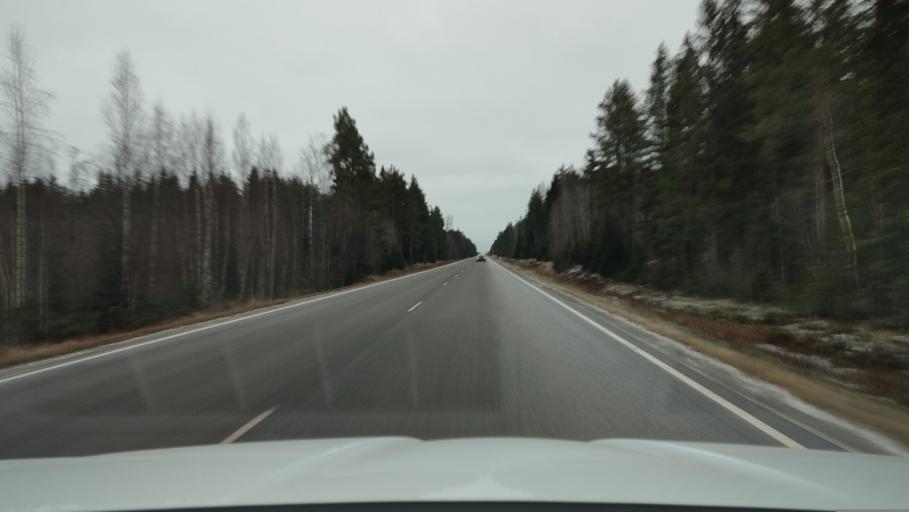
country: FI
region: Ostrobothnia
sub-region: Sydosterbotten
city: Naerpes
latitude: 62.5901
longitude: 21.5004
